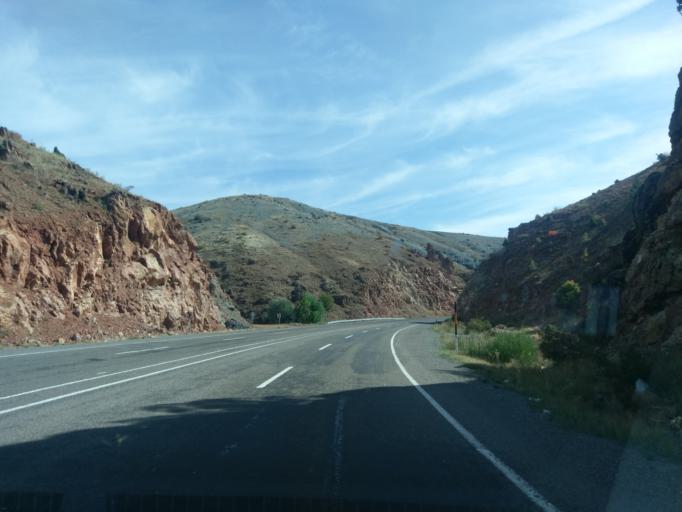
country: TR
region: Sivas
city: Imranli
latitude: 39.8596
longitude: 38.3175
